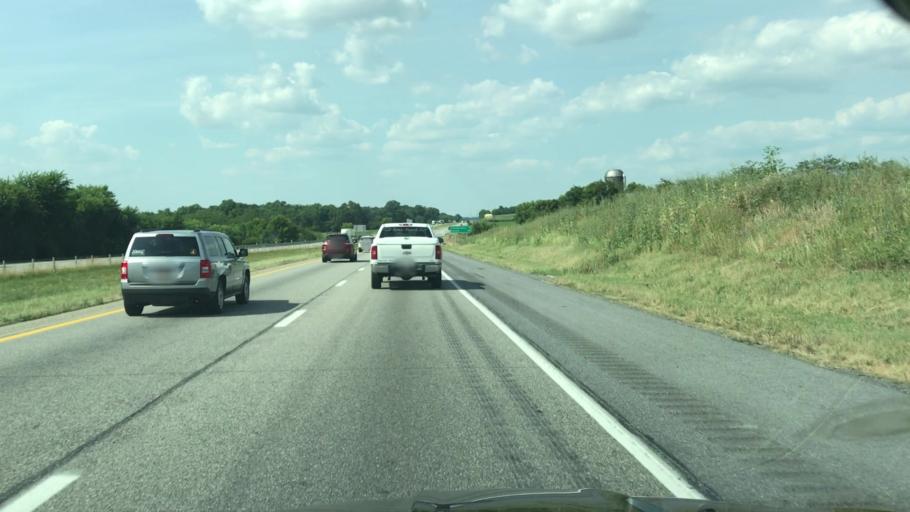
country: US
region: Pennsylvania
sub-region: Franklin County
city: Greencastle
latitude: 39.7954
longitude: -77.7106
